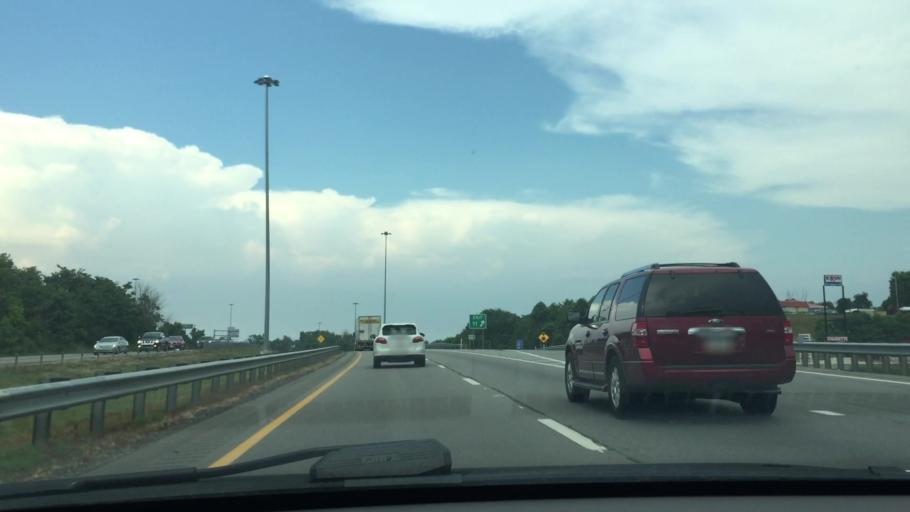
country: US
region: West Virginia
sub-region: Ohio County
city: West Liberty
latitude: 40.0653
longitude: -80.5732
